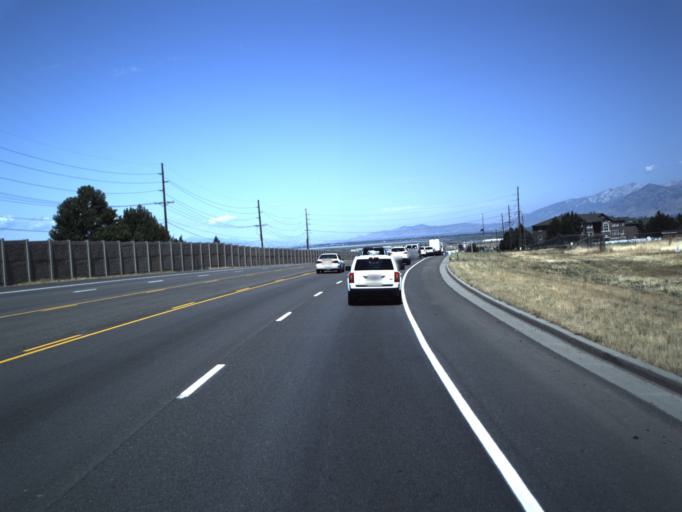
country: US
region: Utah
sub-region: Utah County
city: Spanish Fork
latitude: 40.1113
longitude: -111.6333
